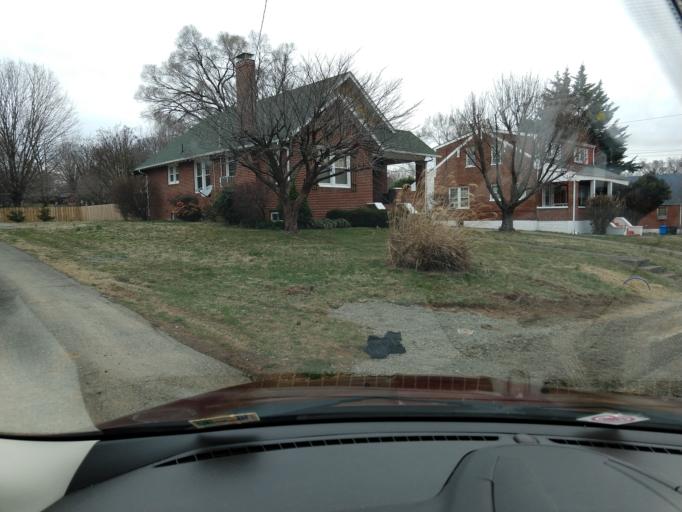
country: US
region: Virginia
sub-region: City of Roanoke
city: Roanoke
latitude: 37.3058
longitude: -79.9394
